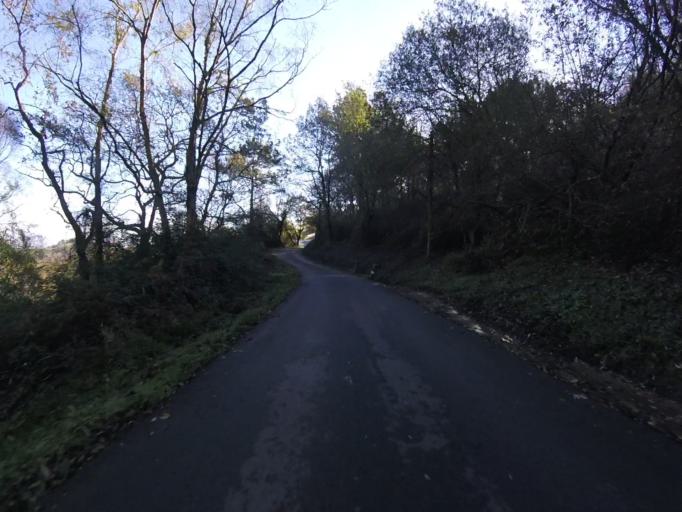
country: ES
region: Basque Country
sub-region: Provincia de Guipuzcoa
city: Usurbil
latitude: 43.2960
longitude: -2.0526
